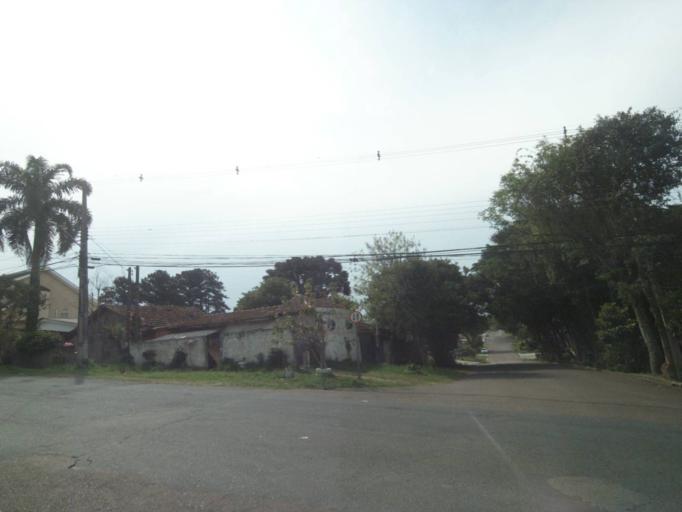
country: BR
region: Parana
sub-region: Pinhais
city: Pinhais
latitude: -25.4064
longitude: -49.2105
